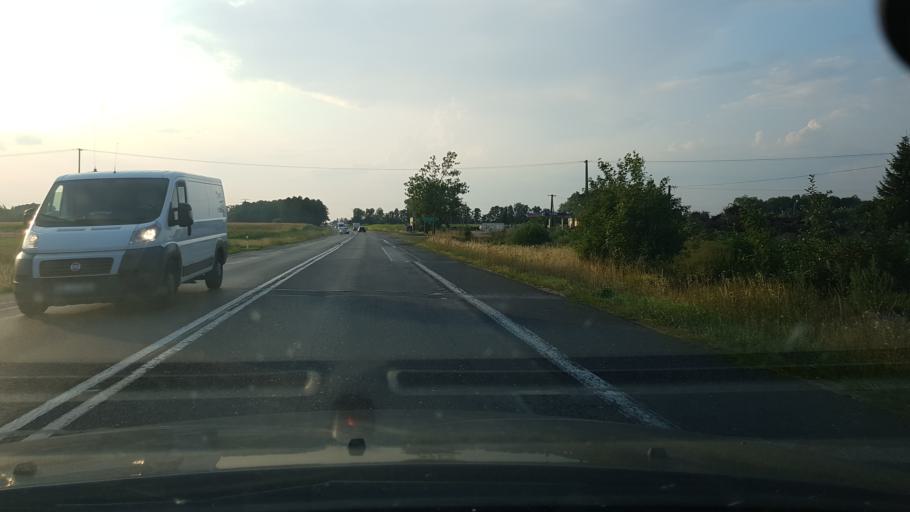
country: PL
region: Masovian Voivodeship
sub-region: Powiat plonski
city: Plonsk
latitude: 52.6765
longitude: 20.3695
